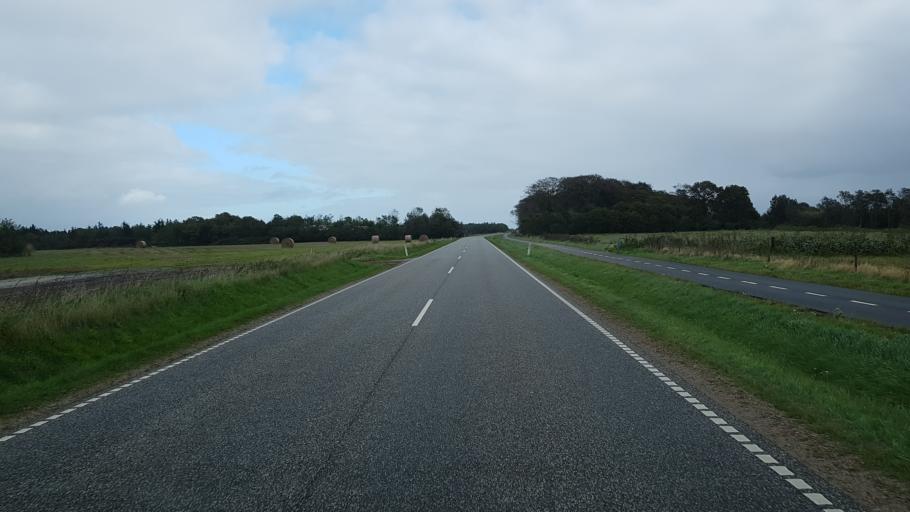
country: DK
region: South Denmark
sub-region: Billund Kommune
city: Grindsted
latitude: 55.7629
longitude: 8.8101
